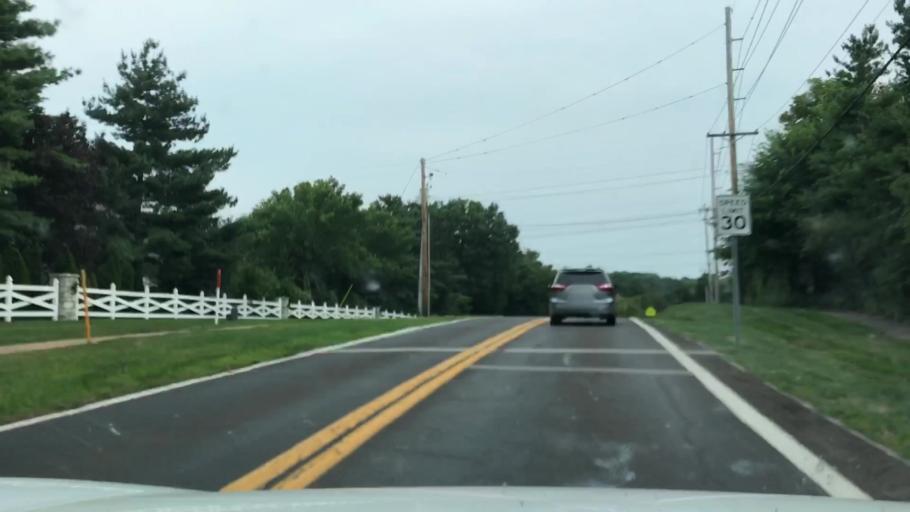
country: US
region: Missouri
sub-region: Saint Louis County
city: Clarkson Valley
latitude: 38.6261
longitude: -90.5914
